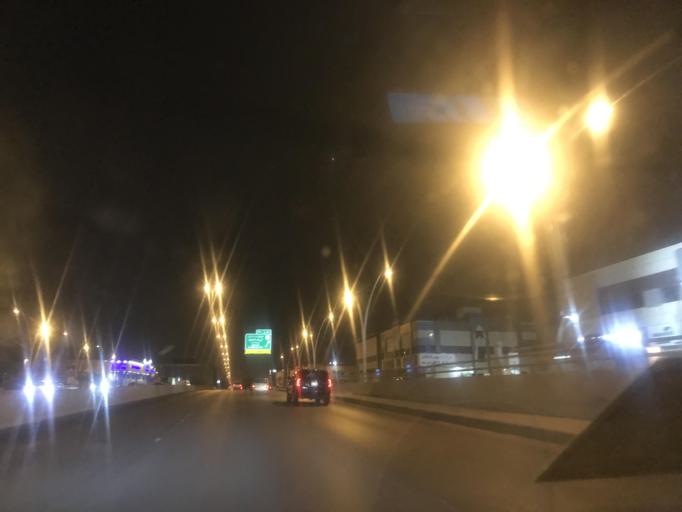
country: SA
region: Ar Riyad
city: Riyadh
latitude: 24.7678
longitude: 46.7105
